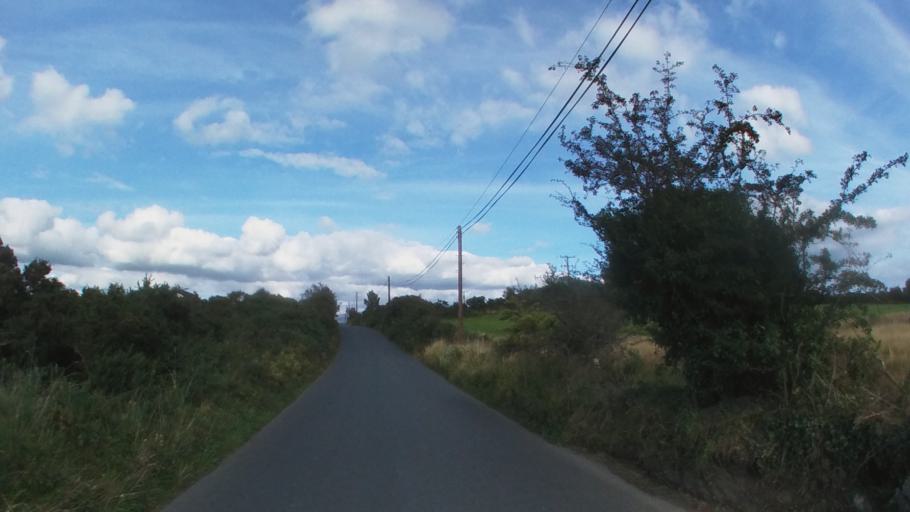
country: GB
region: Northern Ireland
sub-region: Down District
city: Warrenpoint
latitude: 54.0827
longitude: -6.2674
